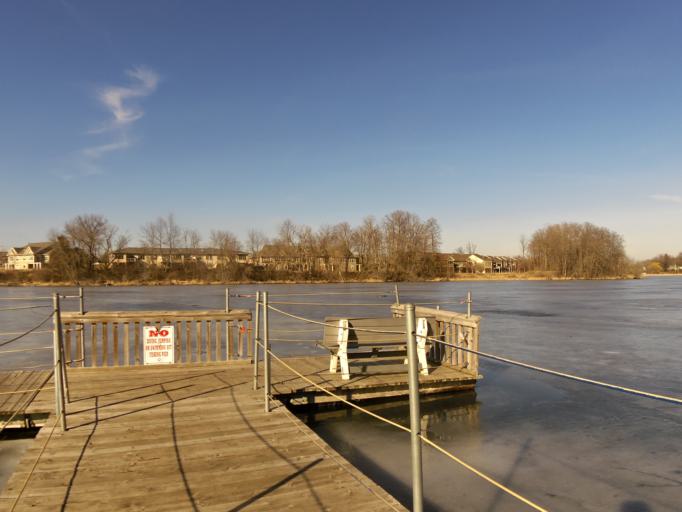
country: US
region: Minnesota
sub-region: Scott County
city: Prior Lake
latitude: 44.7006
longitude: -93.4406
